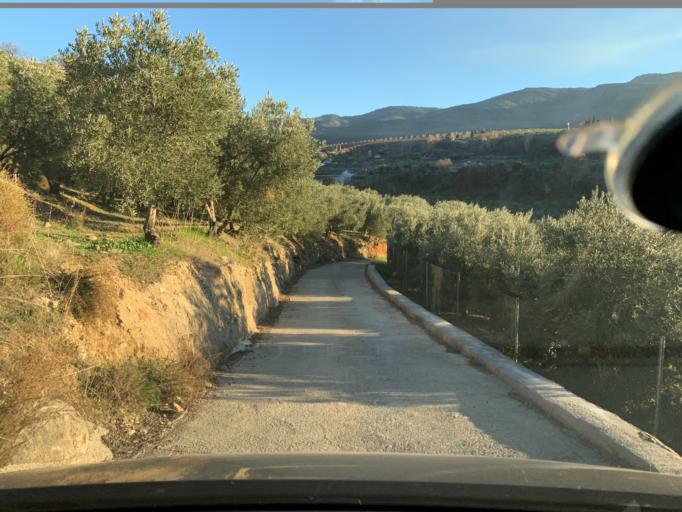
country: ES
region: Andalusia
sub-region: Provincia de Granada
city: Dilar
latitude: 37.0753
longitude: -3.5923
